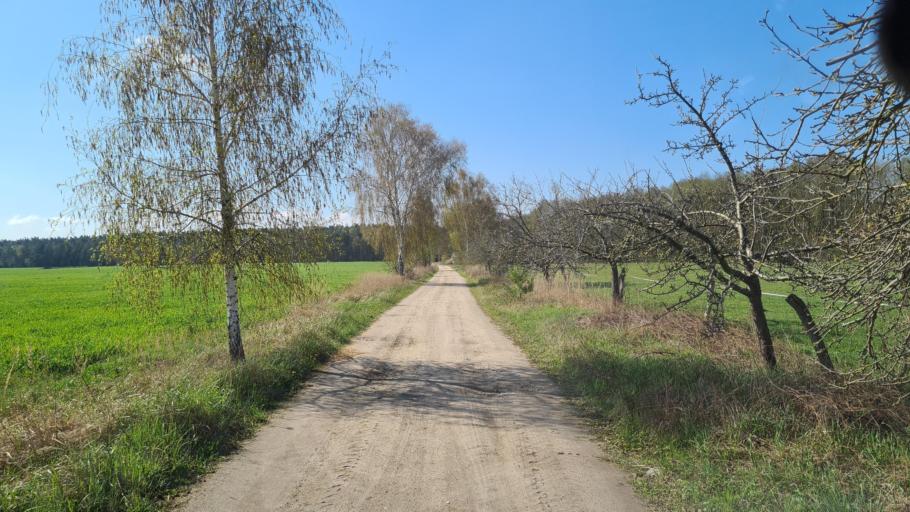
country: DE
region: Brandenburg
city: Altdobern
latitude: 51.7025
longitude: 14.0452
